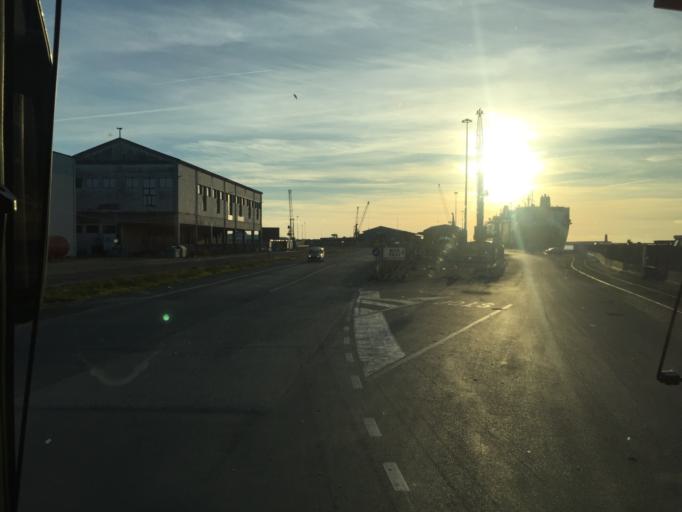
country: IT
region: Tuscany
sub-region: Provincia di Livorno
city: Livorno
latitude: 43.5580
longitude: 10.3022
